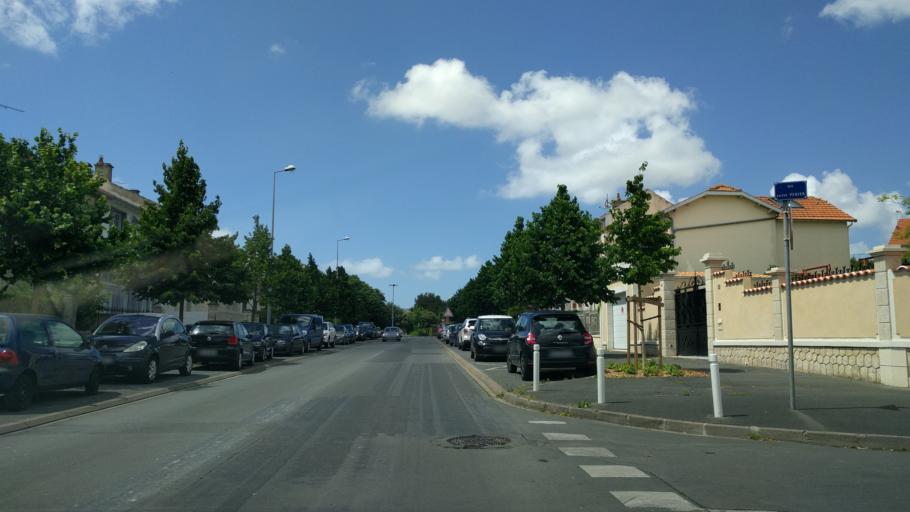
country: FR
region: Poitou-Charentes
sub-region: Departement de la Charente-Maritime
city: La Rochelle
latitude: 46.1629
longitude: -1.1398
